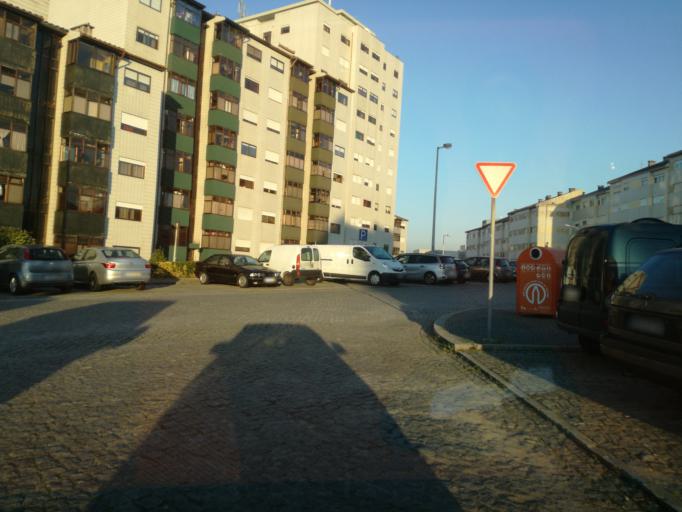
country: PT
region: Porto
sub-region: Maia
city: Leca do Bailio
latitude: 41.2237
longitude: -8.6090
